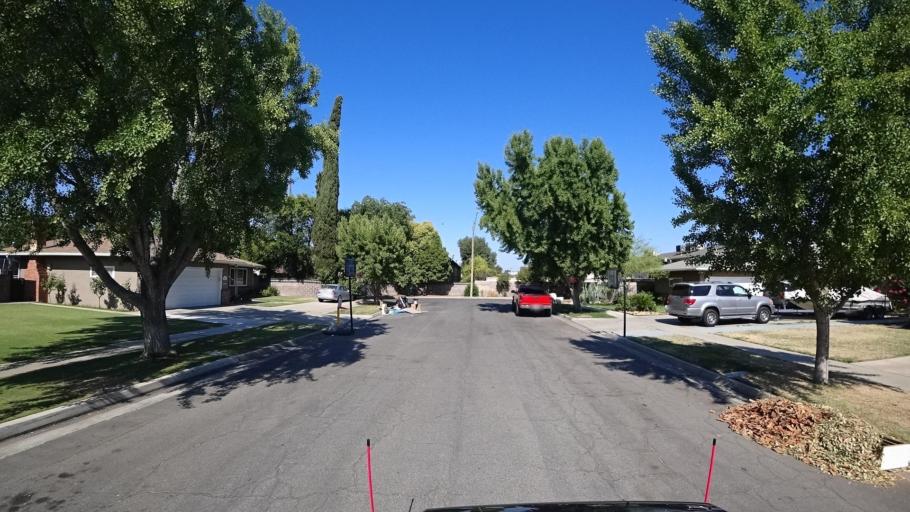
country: US
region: California
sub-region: Fresno County
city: Fresno
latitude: 36.7823
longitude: -119.7518
